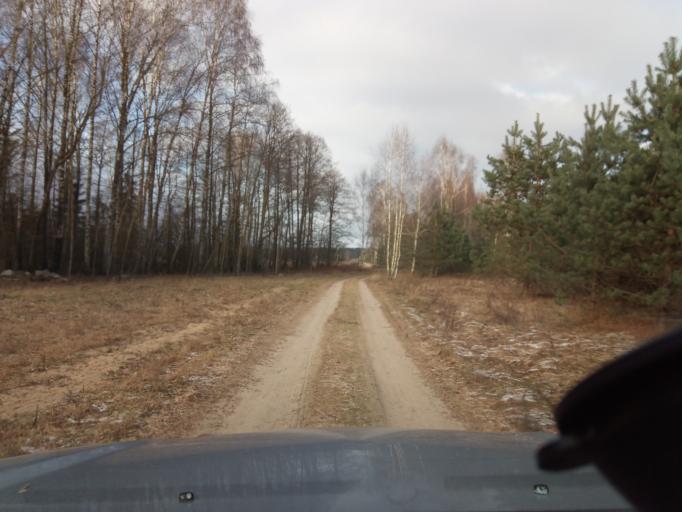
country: LT
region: Alytaus apskritis
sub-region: Alytaus rajonas
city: Daugai
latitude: 54.1112
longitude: 24.2400
